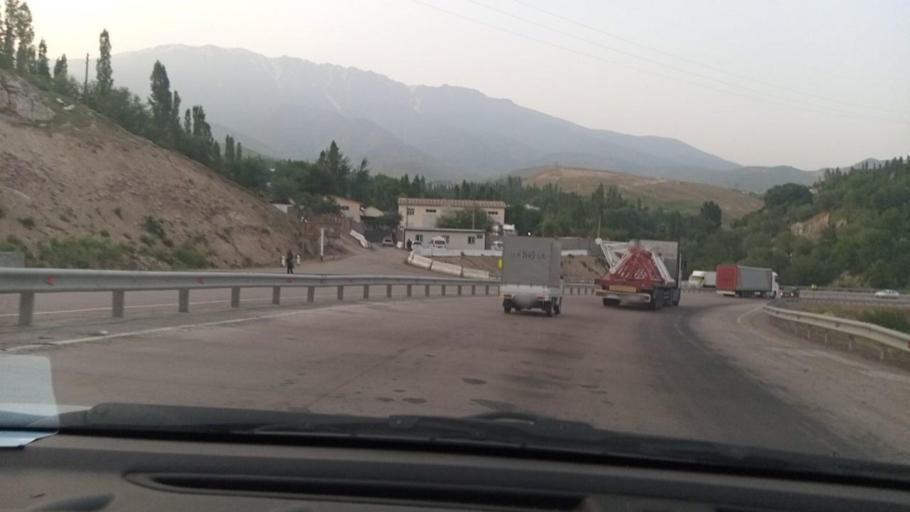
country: UZ
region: Toshkent
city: Angren
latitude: 41.0739
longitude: 70.2516
